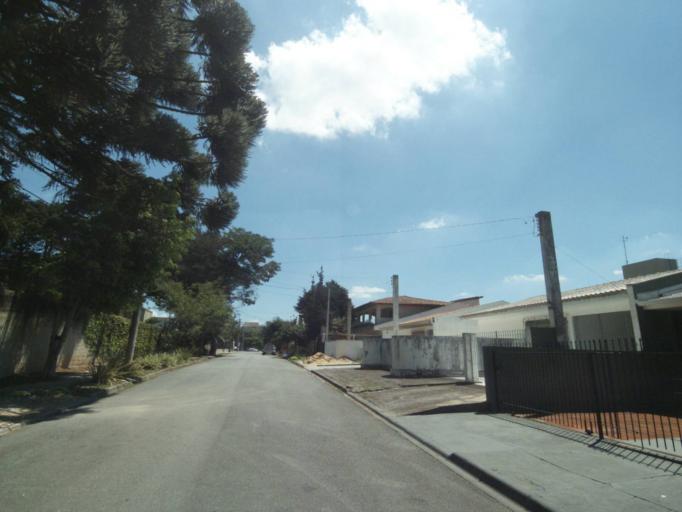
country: BR
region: Parana
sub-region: Curitiba
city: Curitiba
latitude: -25.3952
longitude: -49.2278
